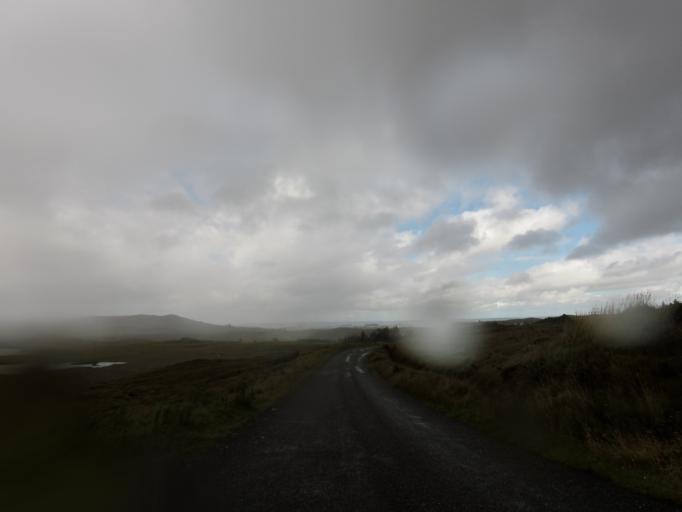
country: IE
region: Connaught
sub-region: County Galway
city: Oughterard
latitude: 53.3971
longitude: -9.3337
